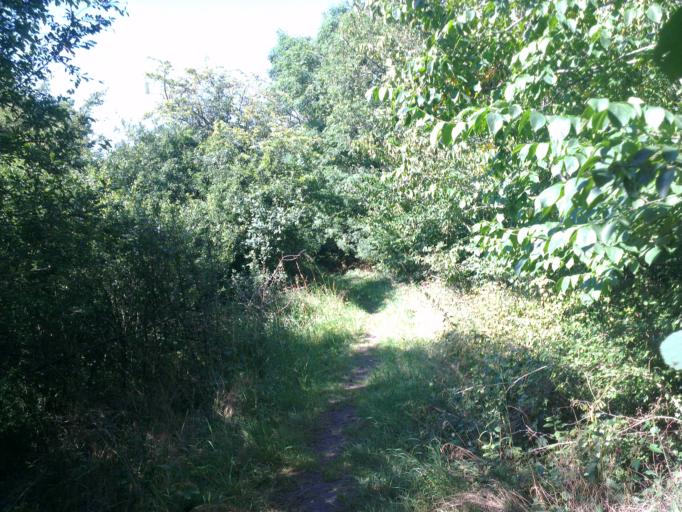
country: DK
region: Capital Region
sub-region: Frederikssund Kommune
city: Skibby
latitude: 55.7700
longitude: 12.0271
